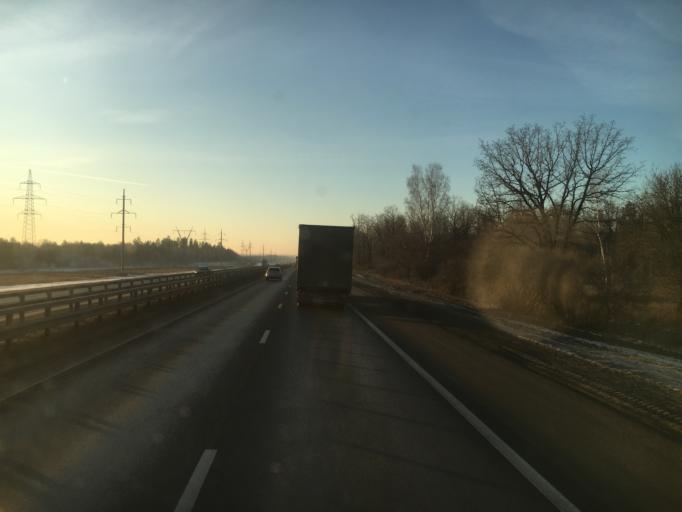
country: RU
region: Samara
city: Pribrezhnyy
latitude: 53.5182
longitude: 49.7981
